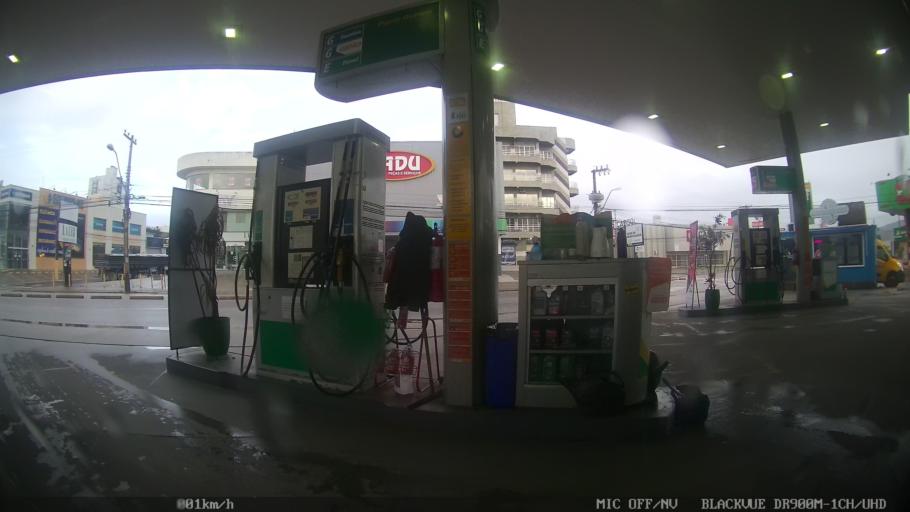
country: BR
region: Santa Catarina
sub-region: Sao Jose
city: Campinas
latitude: -27.5674
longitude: -48.6114
